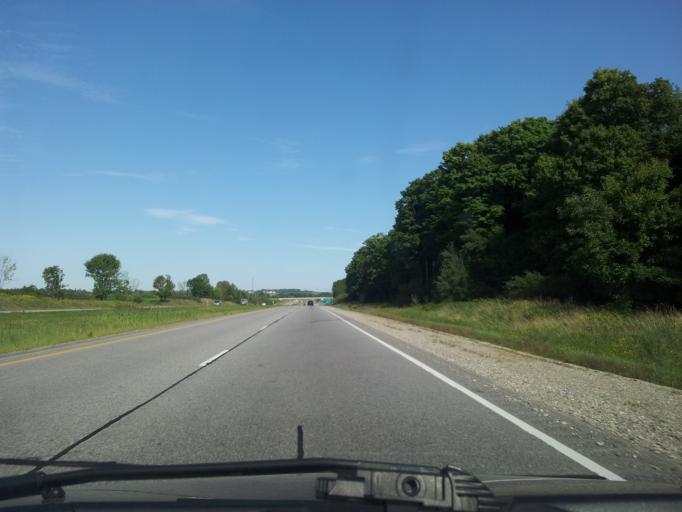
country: CA
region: Ontario
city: Kitchener
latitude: 43.4021
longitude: -80.6116
